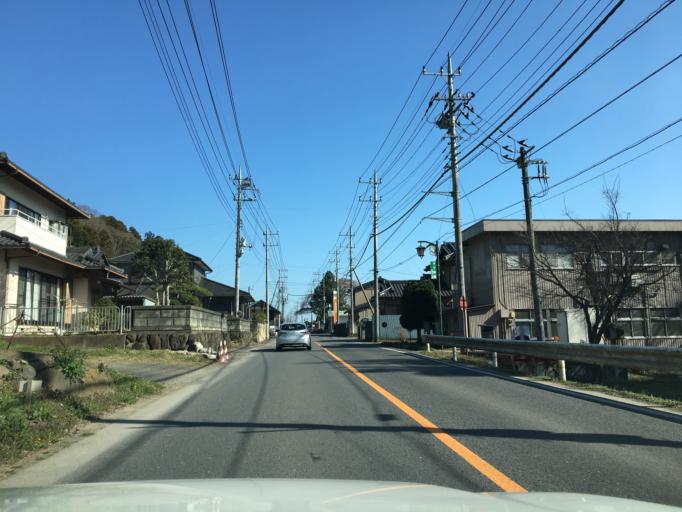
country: JP
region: Ibaraki
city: Omiya
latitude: 36.5523
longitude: 140.3237
